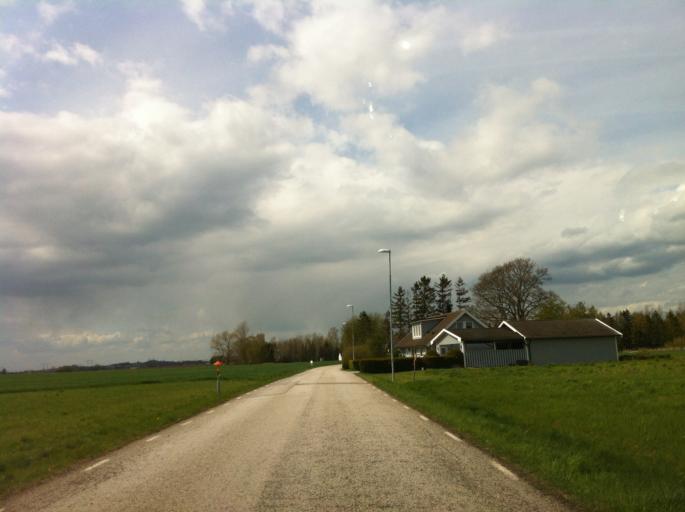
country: SE
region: Skane
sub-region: Kavlinge Kommun
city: Kaevlinge
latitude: 55.8088
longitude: 13.1481
